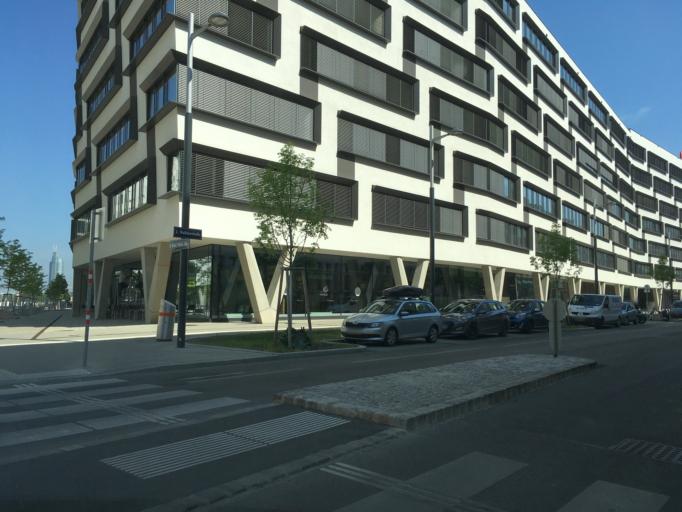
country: AT
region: Vienna
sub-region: Wien Stadt
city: Vienna
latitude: 48.2220
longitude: 16.3943
